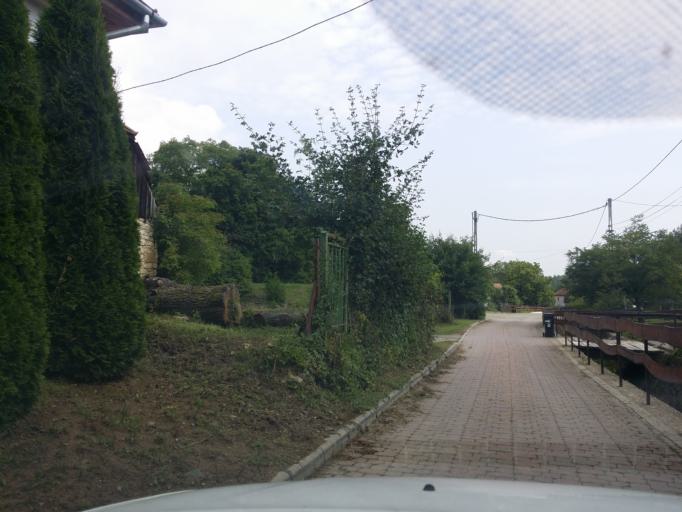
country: HU
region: Borsod-Abauj-Zemplen
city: Satoraljaujhely
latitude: 48.4583
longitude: 21.5855
